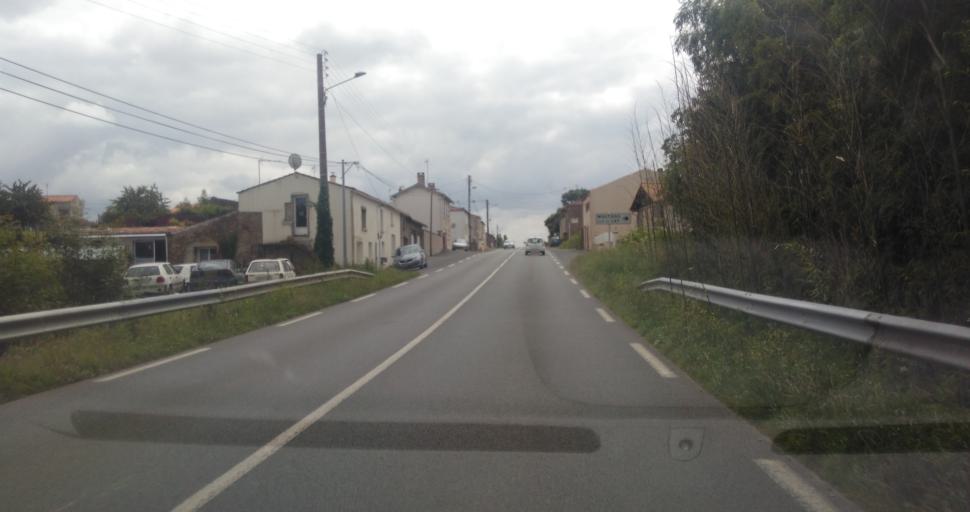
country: FR
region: Pays de la Loire
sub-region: Departement de la Vendee
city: Bournezeau
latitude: 46.6174
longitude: -1.1512
